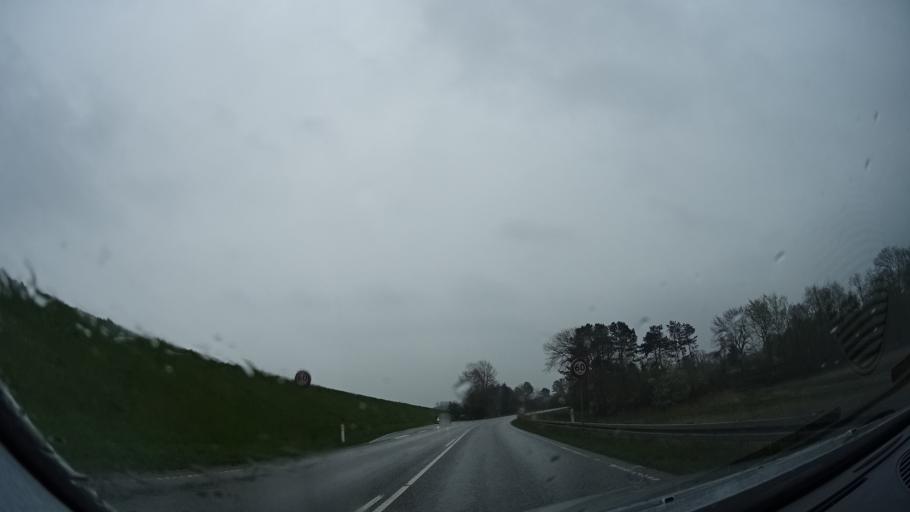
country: DK
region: Zealand
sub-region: Holbaek Kommune
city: Holbaek
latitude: 55.7738
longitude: 11.6245
